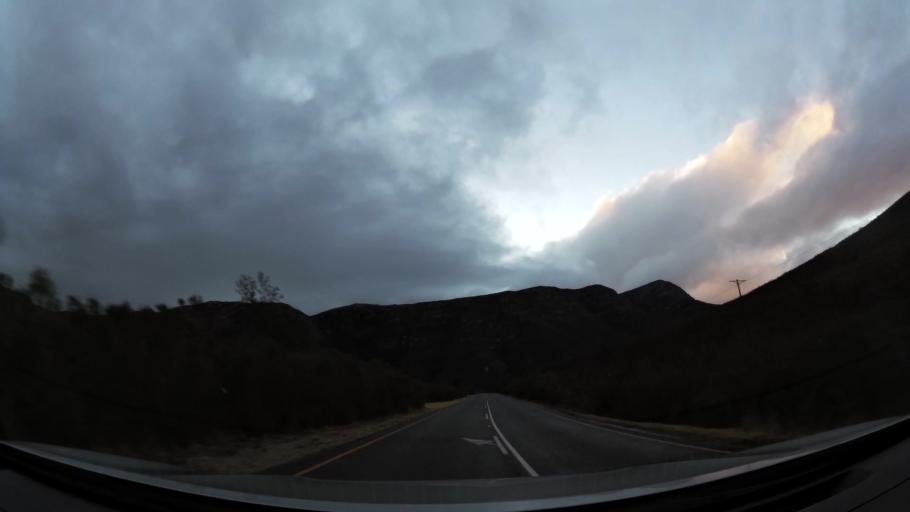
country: ZA
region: Western Cape
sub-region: Overberg District Municipality
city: Swellendam
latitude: -33.9764
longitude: 20.7035
